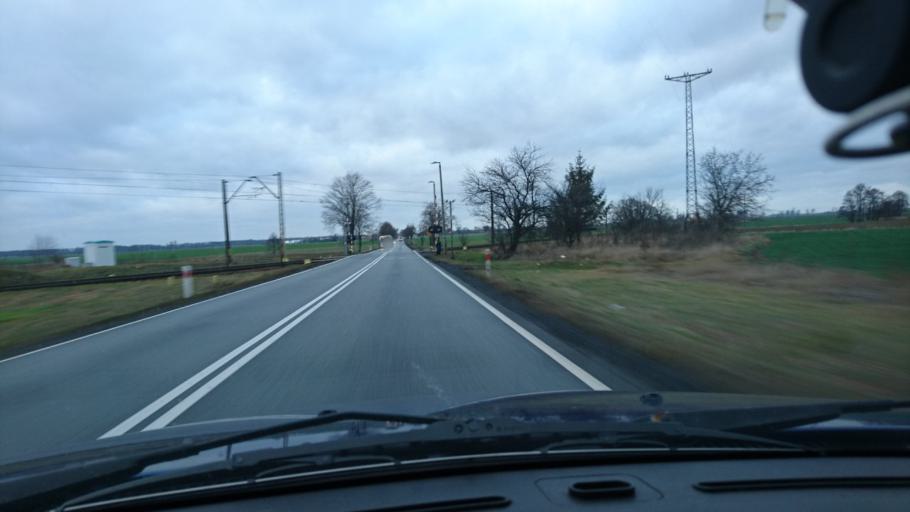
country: PL
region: Opole Voivodeship
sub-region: Powiat kluczborski
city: Kluczbork
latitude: 51.0155
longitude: 18.2003
